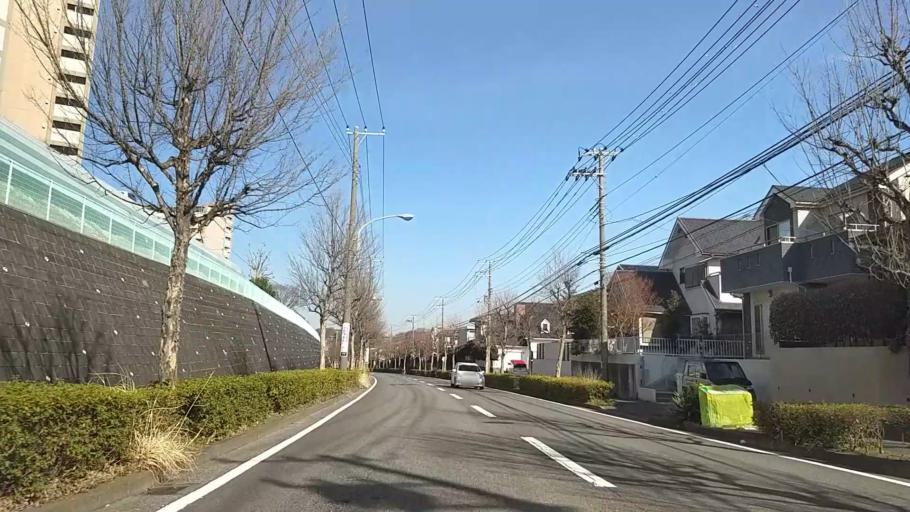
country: JP
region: Kanagawa
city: Kamakura
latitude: 35.3766
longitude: 139.5855
